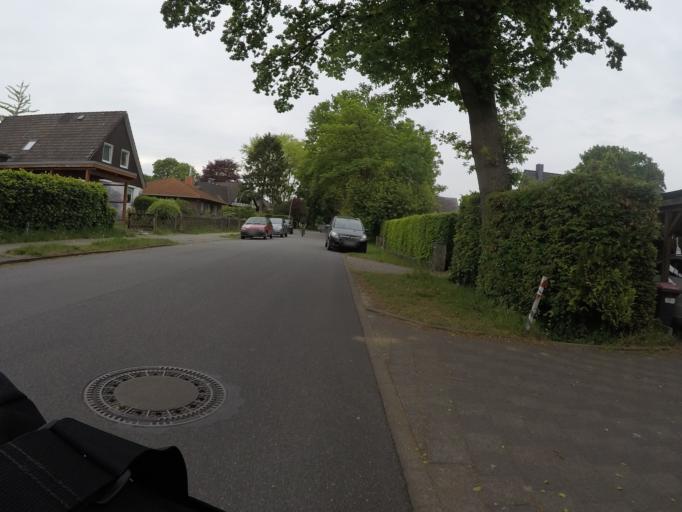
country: DE
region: Hamburg
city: Hamburg-Nord
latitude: 53.6200
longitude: 9.9599
